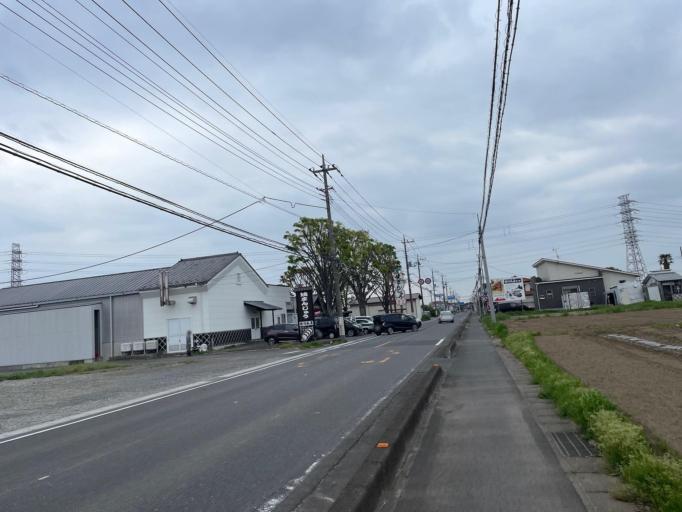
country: JP
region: Gunma
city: Sakai-nakajima
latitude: 36.2753
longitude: 139.2236
